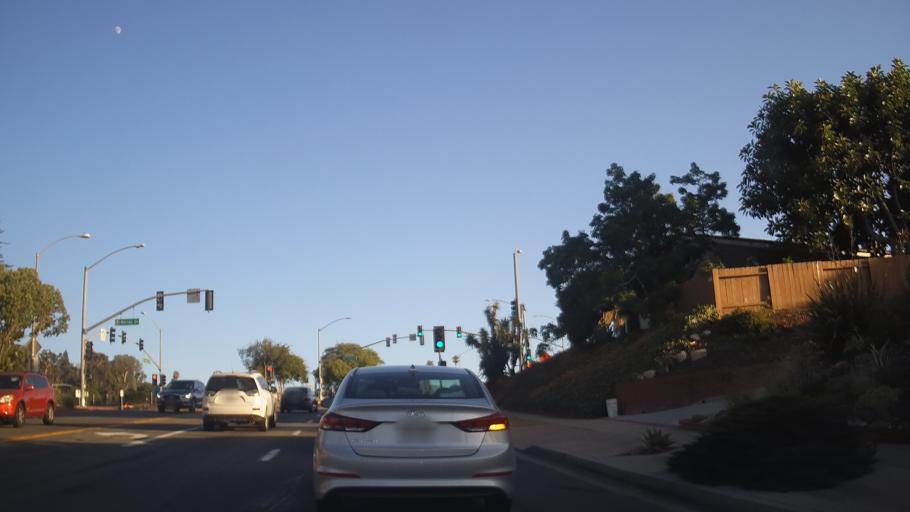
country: US
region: California
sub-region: San Diego County
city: La Mesa
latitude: 32.7809
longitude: -116.9972
